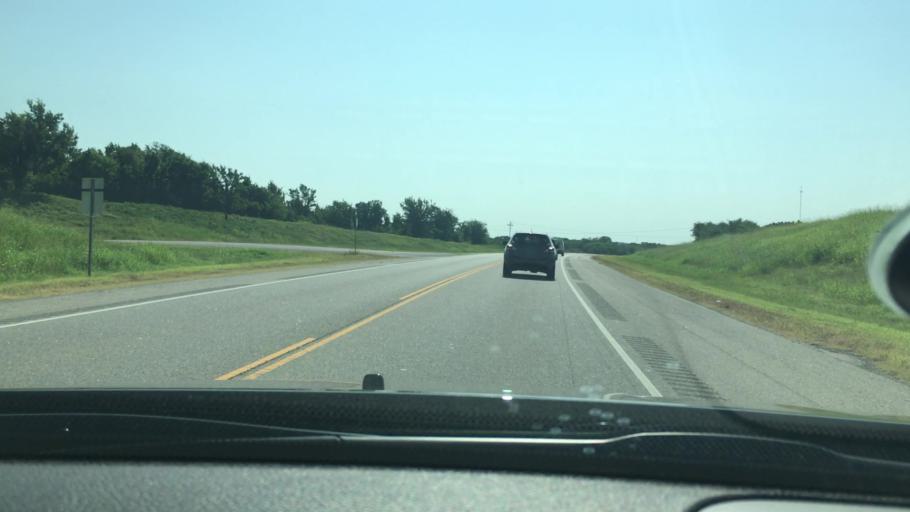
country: US
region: Oklahoma
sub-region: Pontotoc County
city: Ada
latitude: 34.6424
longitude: -96.4963
